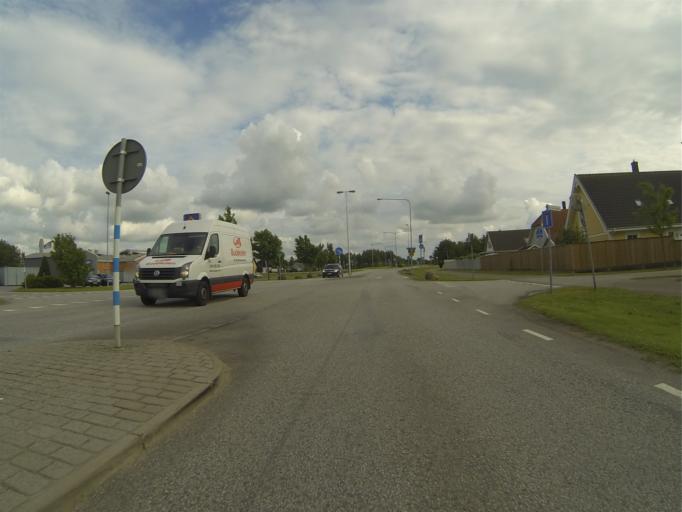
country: SE
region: Skane
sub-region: Staffanstorps Kommun
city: Staffanstorp
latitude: 55.6430
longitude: 13.2285
